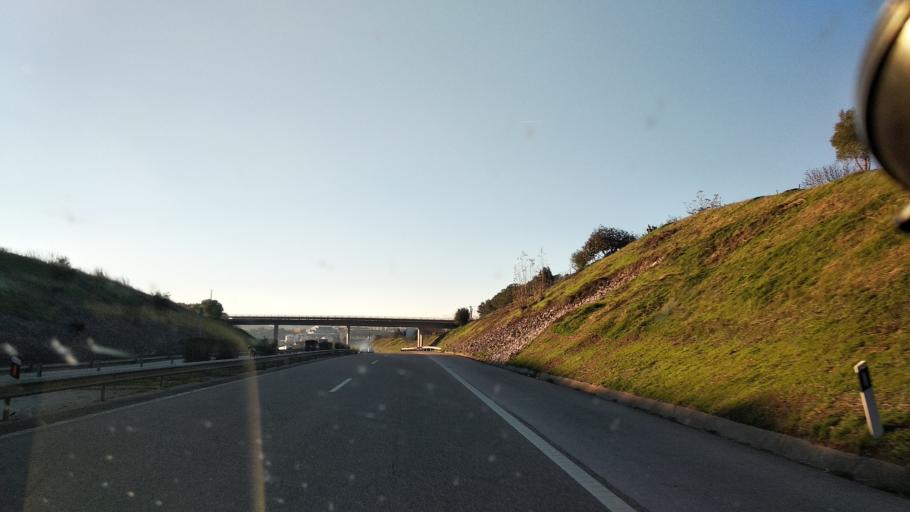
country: PT
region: Santarem
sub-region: Torres Novas
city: Riachos
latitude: 39.4691
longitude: -8.5126
